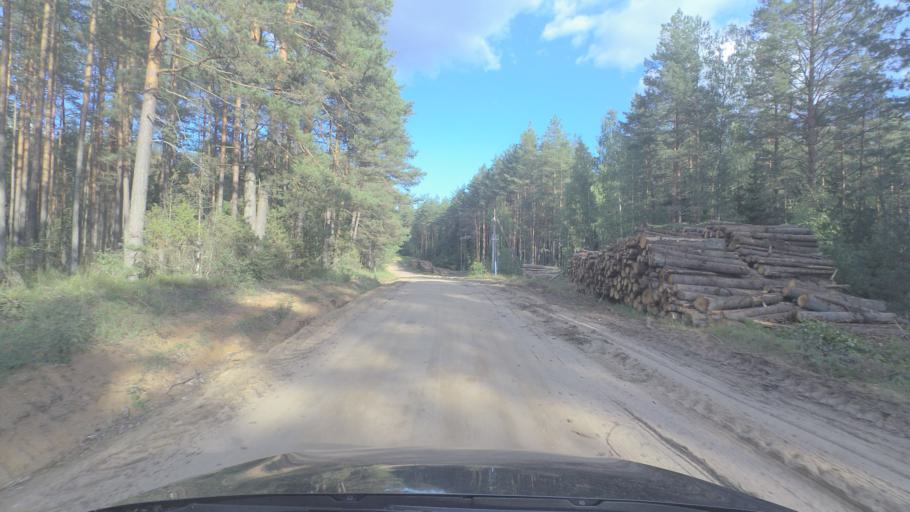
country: LT
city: Pabrade
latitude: 55.1538
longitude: 25.7807
